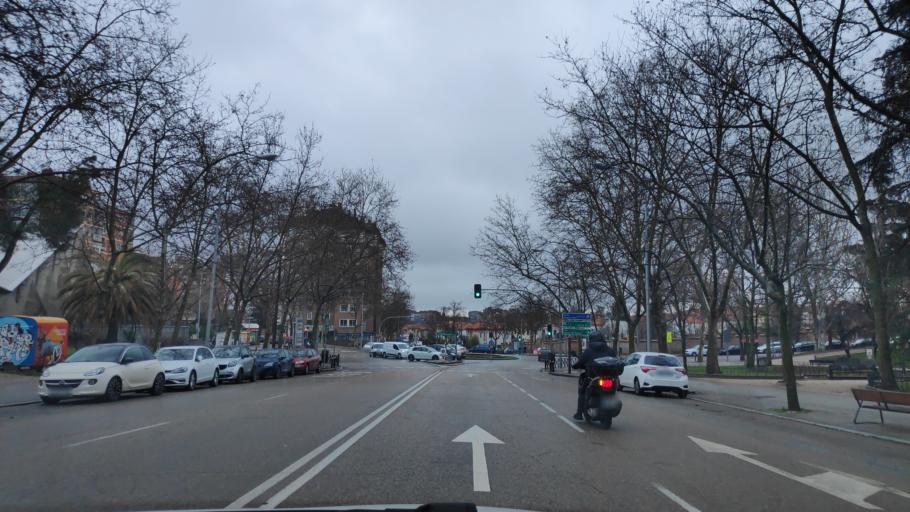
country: ES
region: Madrid
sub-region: Provincia de Madrid
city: Chamartin
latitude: 40.4516
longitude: -3.6757
